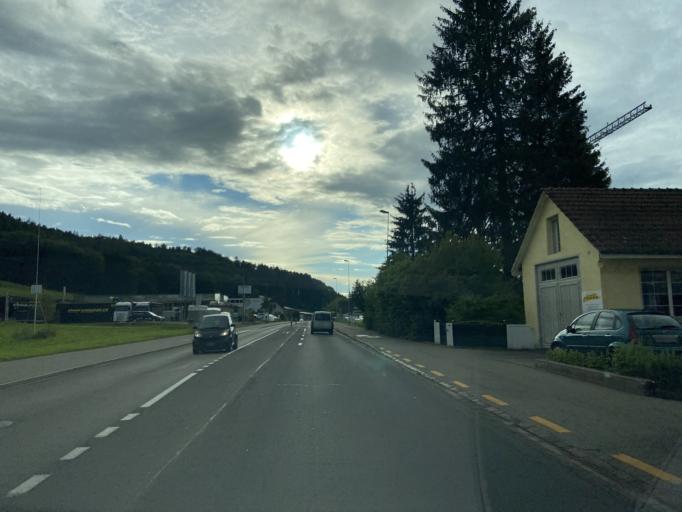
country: CH
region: Zurich
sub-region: Bezirk Winterthur
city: Elsau-Raeterschen / Raeterschen
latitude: 47.4990
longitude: 8.7923
